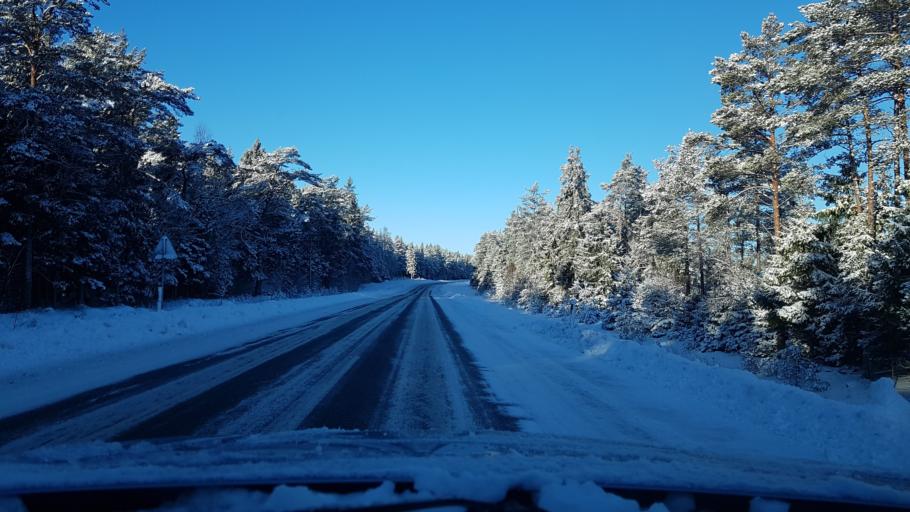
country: EE
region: Hiiumaa
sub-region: Kaerdla linn
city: Kardla
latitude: 58.9640
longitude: 22.8398
